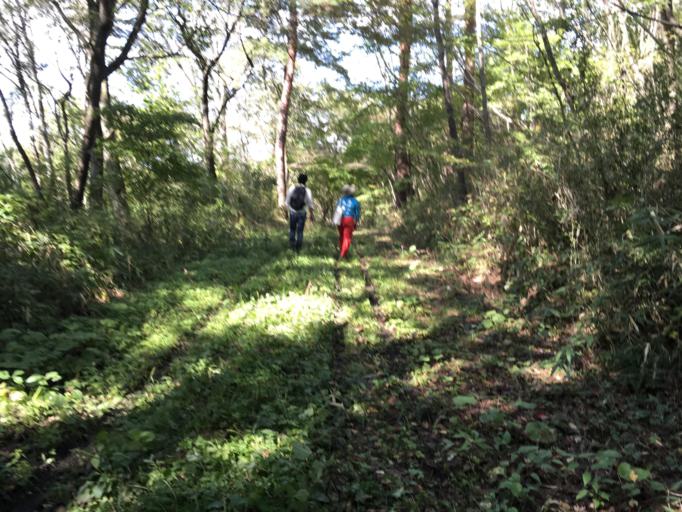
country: JP
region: Iwate
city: Ichinoseki
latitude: 38.8822
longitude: 141.1254
